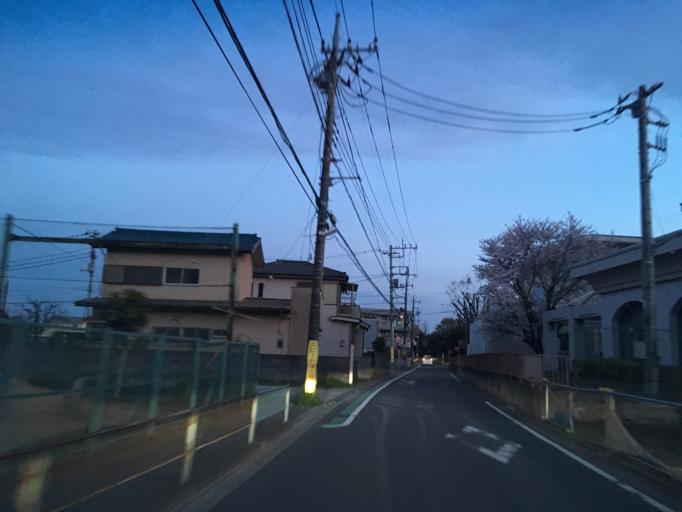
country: JP
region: Saitama
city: Sayama
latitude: 35.8027
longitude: 139.4019
